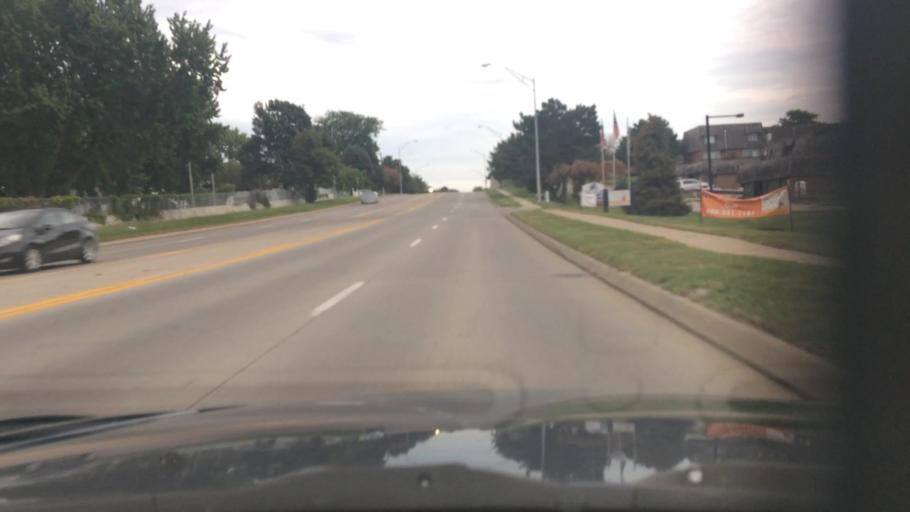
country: US
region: Nebraska
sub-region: Douglas County
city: Ralston
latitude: 41.2052
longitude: -96.0501
